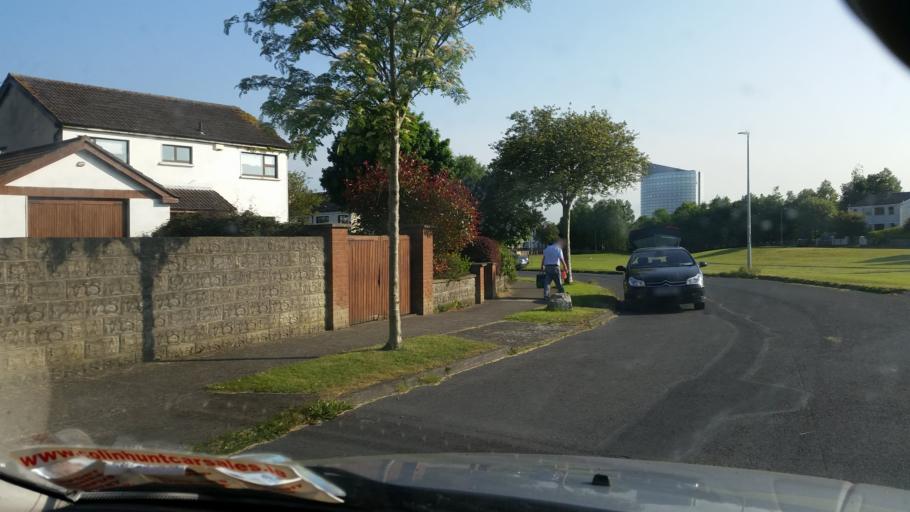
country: IE
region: Leinster
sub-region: Fingal County
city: Blanchardstown
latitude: 53.3975
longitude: -6.3821
